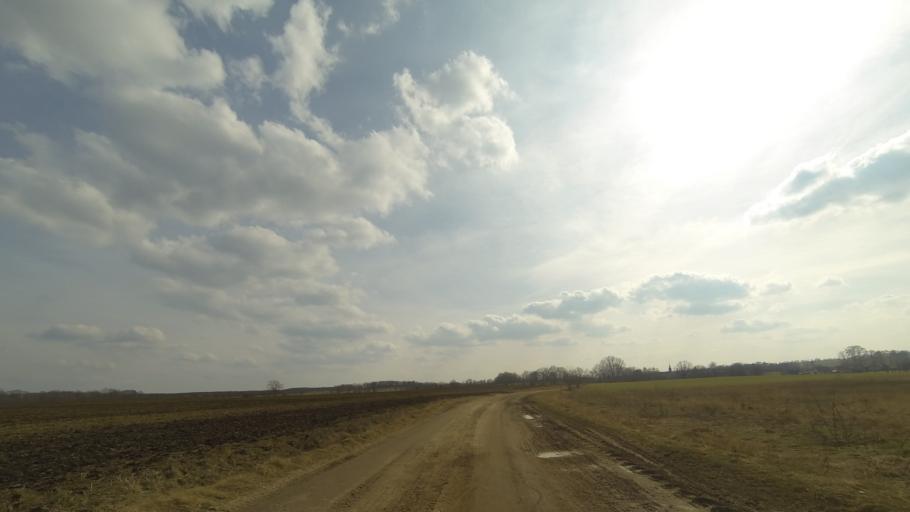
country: DE
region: Saxony
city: Radeburg
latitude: 51.2455
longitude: 13.7054
